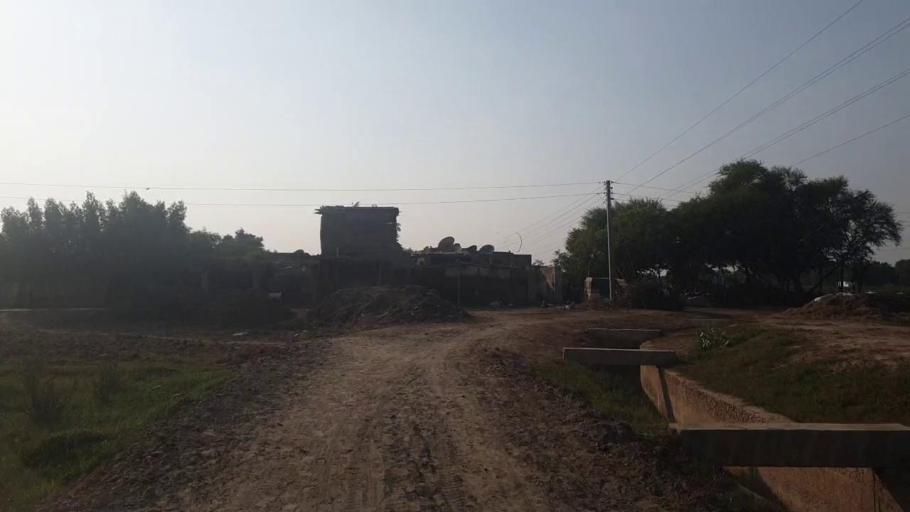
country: PK
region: Sindh
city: Tando Jam
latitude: 25.4267
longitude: 68.4654
